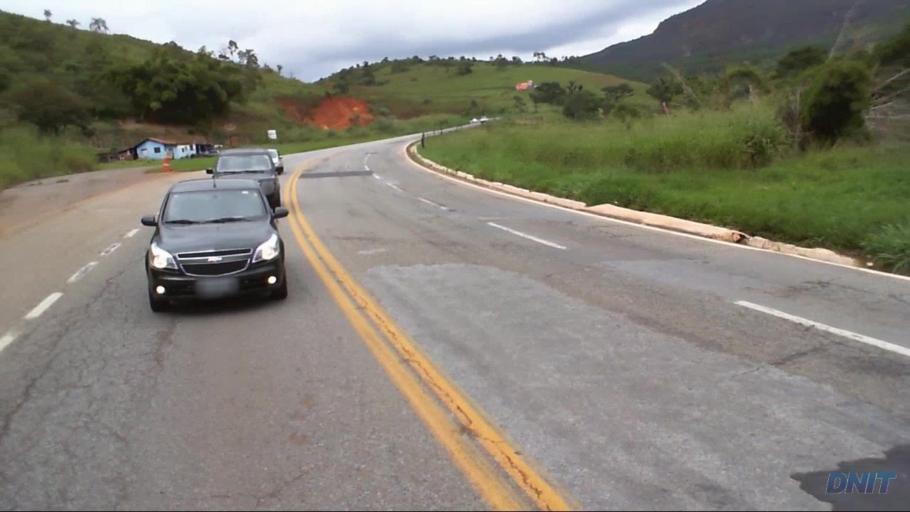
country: BR
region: Minas Gerais
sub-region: Barao De Cocais
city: Barao de Cocais
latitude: -19.8327
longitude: -43.3742
